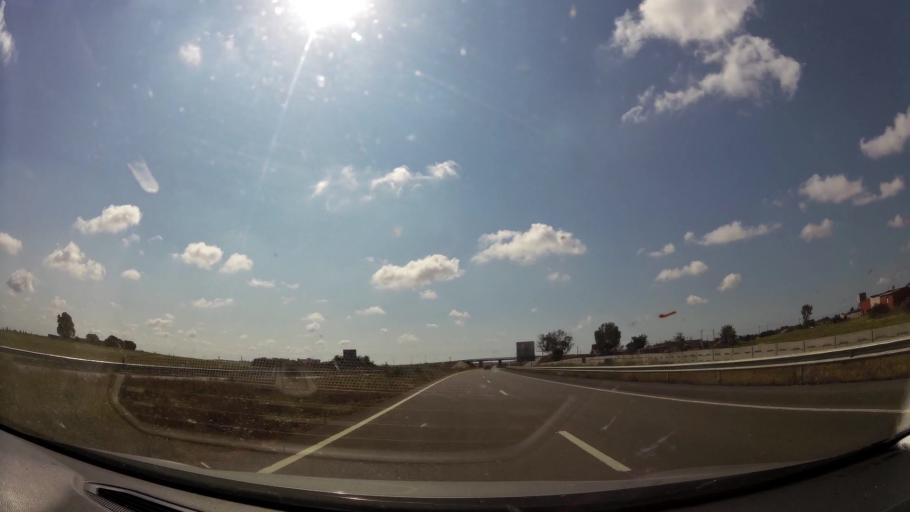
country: MA
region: Rabat-Sale-Zemmour-Zaer
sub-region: Skhirate-Temara
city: Temara
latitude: 33.8387
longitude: -6.8806
